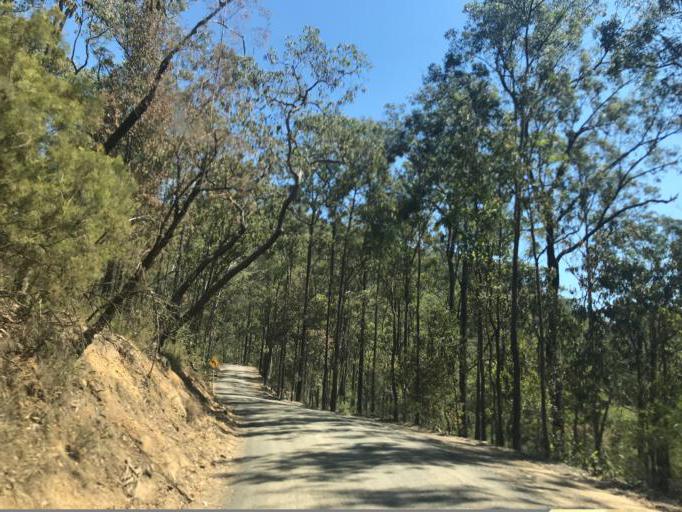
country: AU
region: New South Wales
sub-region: Wyong Shire
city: Little Jilliby
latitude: -33.1878
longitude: 151.0503
